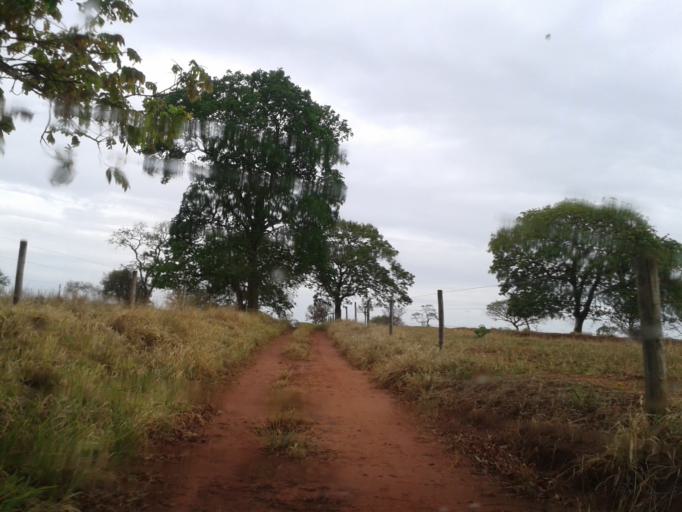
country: BR
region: Minas Gerais
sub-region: Campina Verde
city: Campina Verde
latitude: -19.3490
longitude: -49.5530
